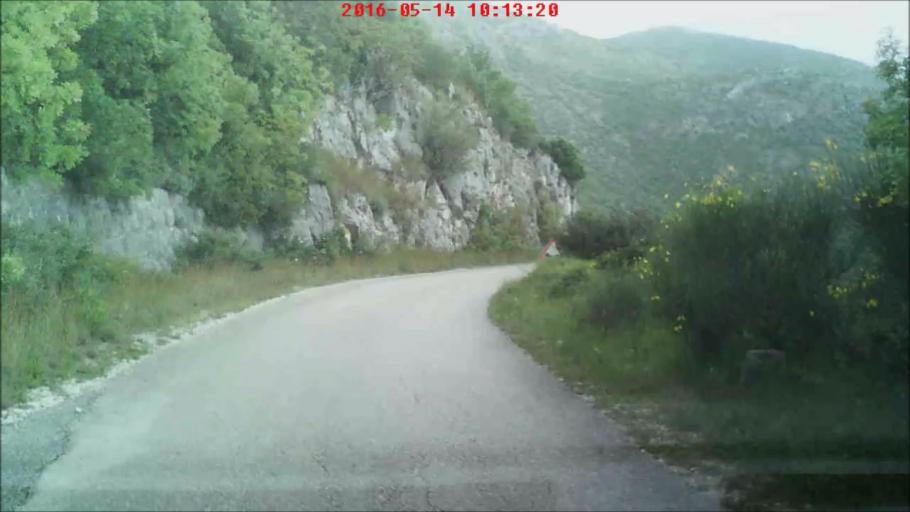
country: HR
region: Dubrovacko-Neretvanska
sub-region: Grad Dubrovnik
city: Mokosica
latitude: 42.7341
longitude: 17.9527
